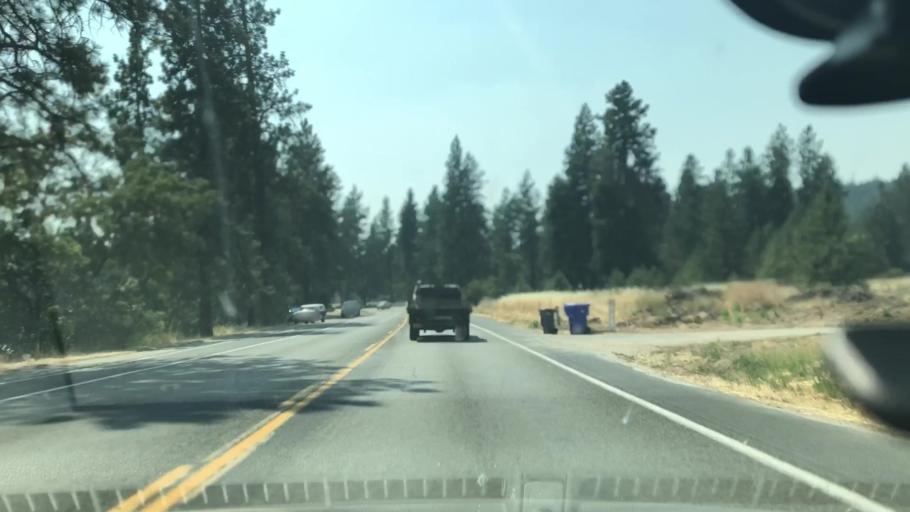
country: US
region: Washington
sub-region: Spokane County
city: Millwood
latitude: 47.6928
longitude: -117.3161
